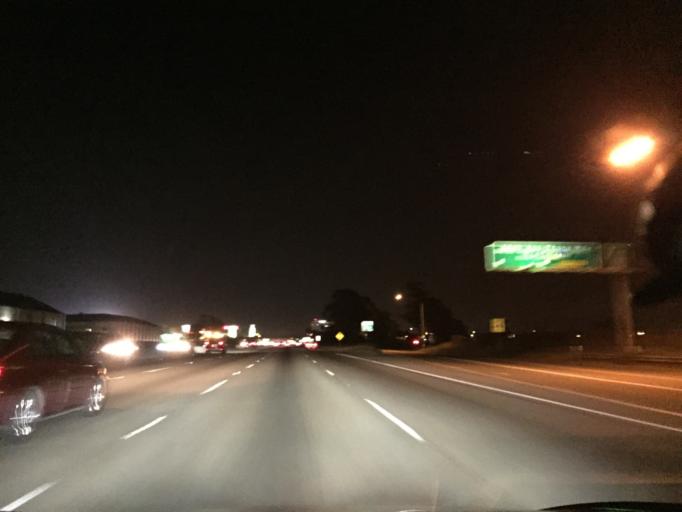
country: US
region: California
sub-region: Alameda County
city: Alameda
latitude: 37.7579
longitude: -122.2118
